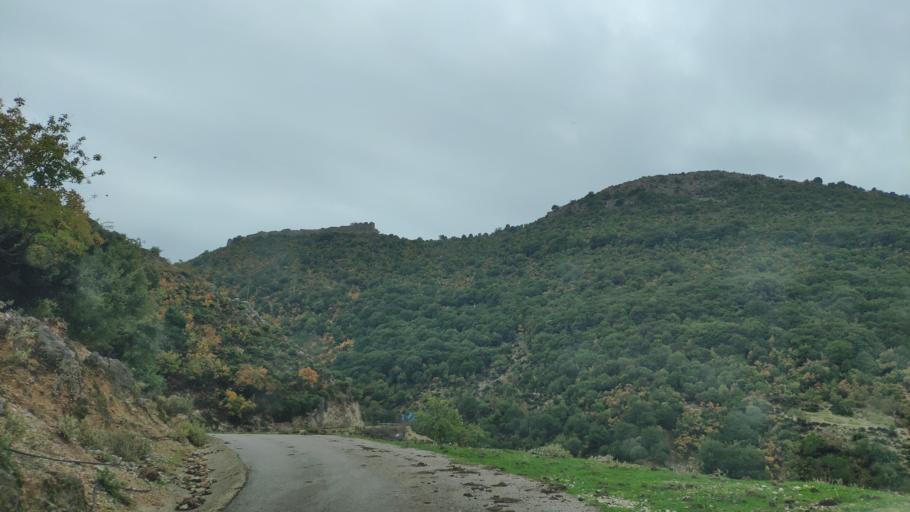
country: GR
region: Epirus
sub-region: Nomos Prevezis
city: Kanalaki
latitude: 39.3420
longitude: 20.6526
